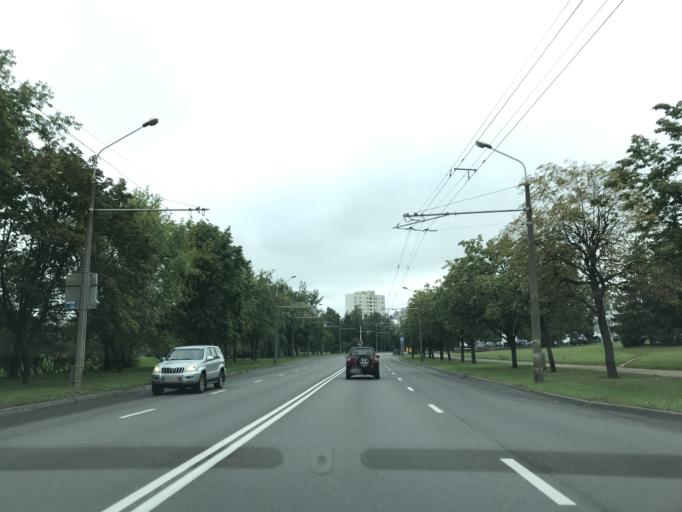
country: BY
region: Minsk
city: Borovlyany
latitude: 53.9405
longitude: 27.6433
